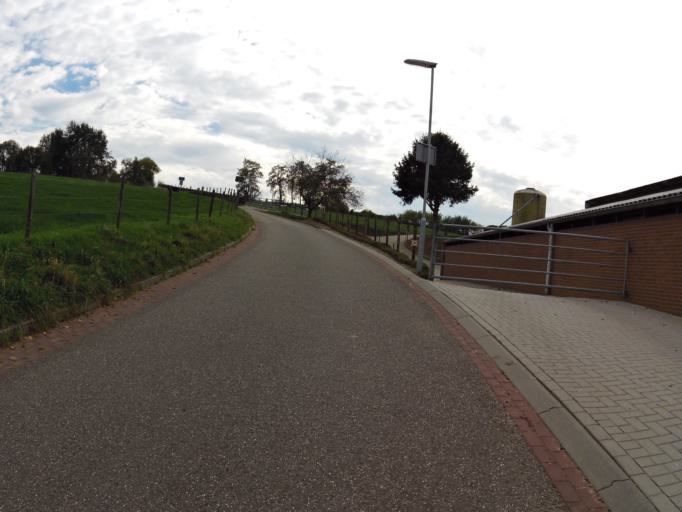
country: NL
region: Limburg
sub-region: Gemeente Voerendaal
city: Ubachsberg
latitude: 50.8234
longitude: 5.9368
